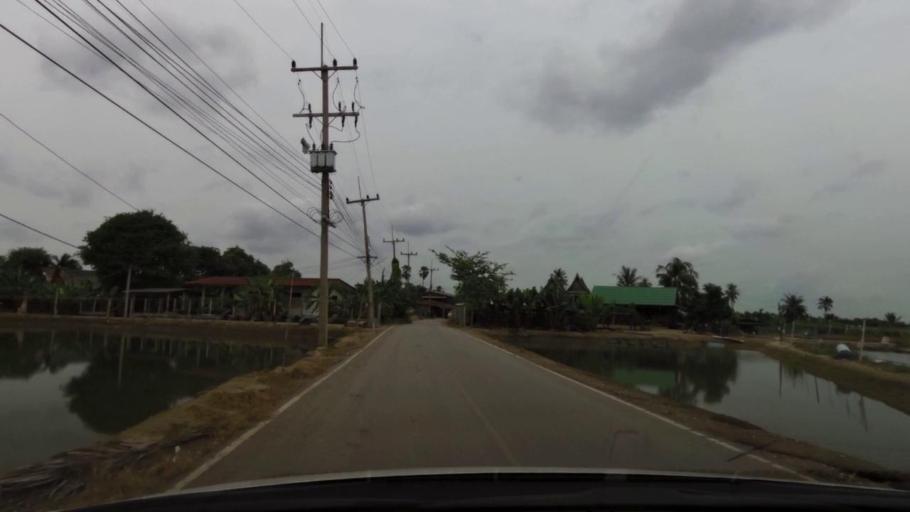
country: TH
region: Samut Sakhon
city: Ban Phaeo
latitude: 13.6266
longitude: 100.0257
